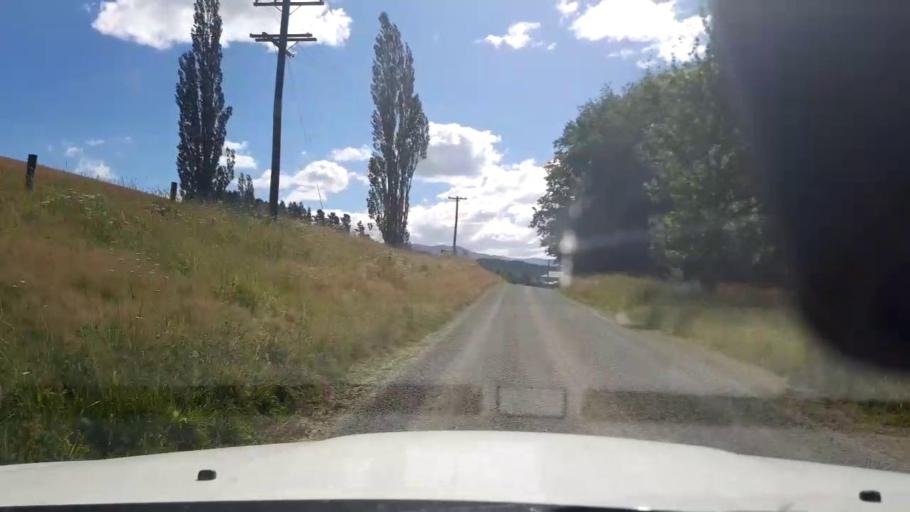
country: NZ
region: Canterbury
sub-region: Timaru District
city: Pleasant Point
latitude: -44.3175
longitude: 170.9381
